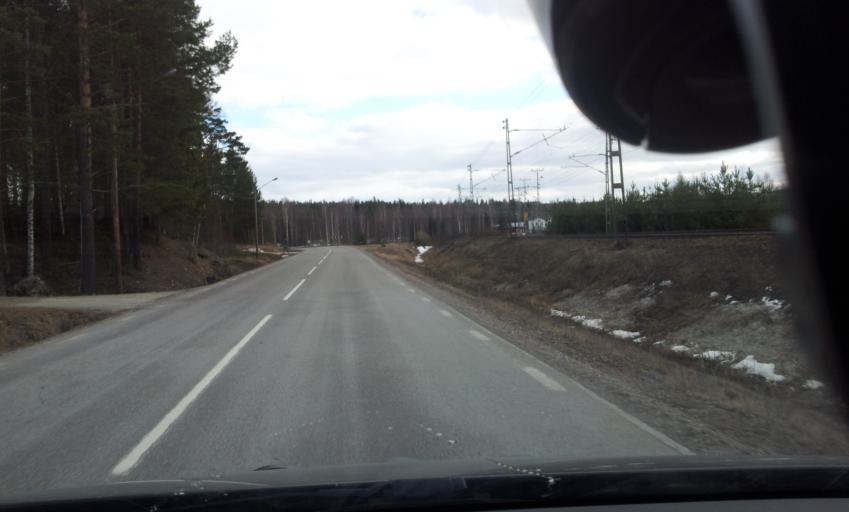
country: SE
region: Vaesternorrland
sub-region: Ange Kommun
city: Ange
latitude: 62.1675
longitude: 15.6762
